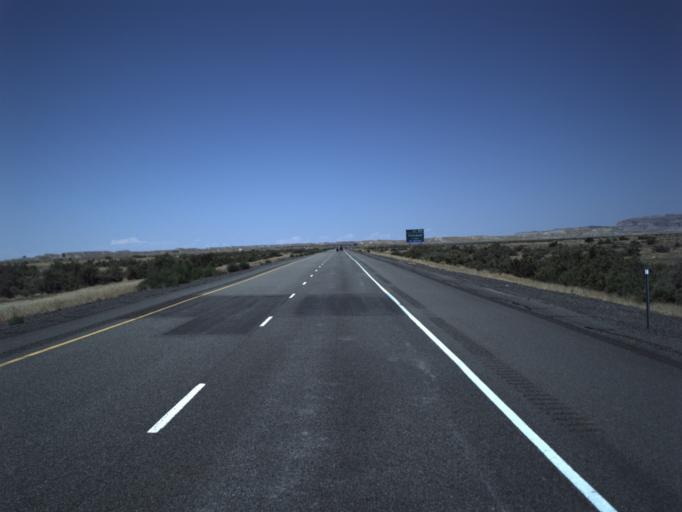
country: US
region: Utah
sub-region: Grand County
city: Moab
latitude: 38.9428
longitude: -109.5891
